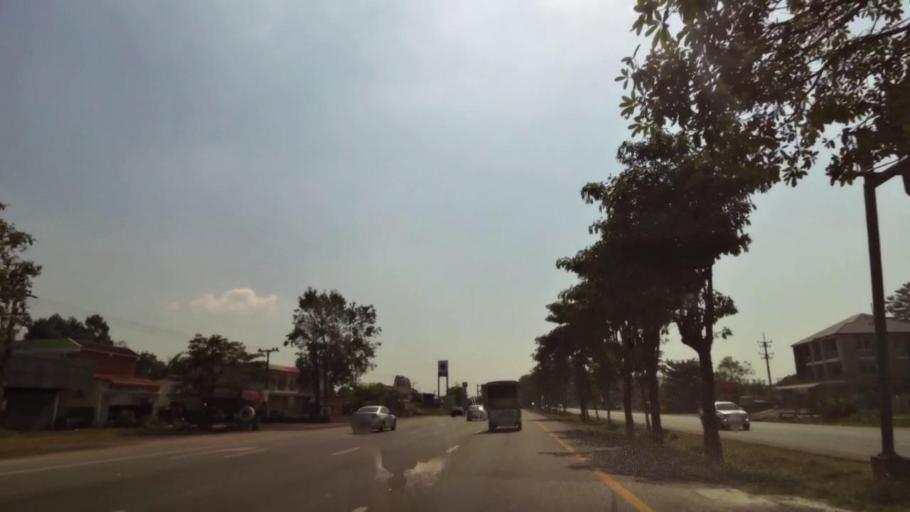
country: TH
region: Phichit
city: Bueng Na Rang
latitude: 16.1208
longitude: 100.1257
